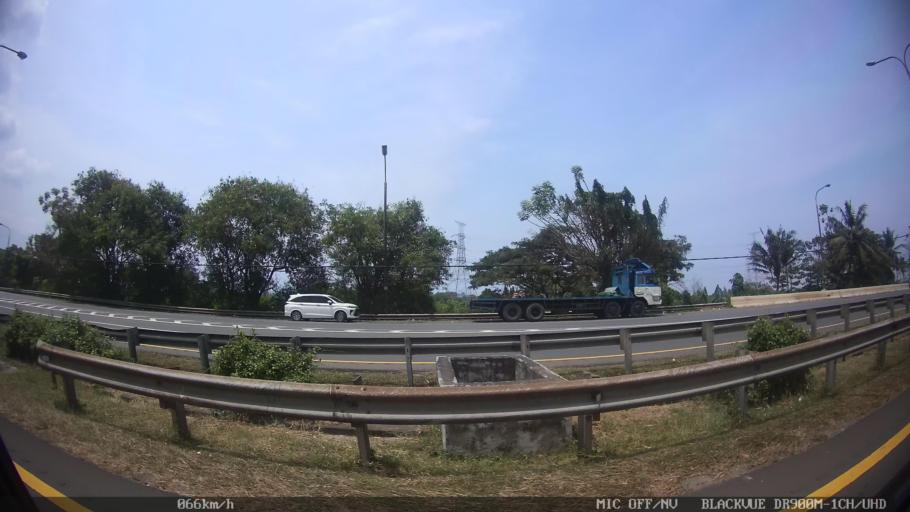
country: ID
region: Banten
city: Bojonegara
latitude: -6.0227
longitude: 106.0933
